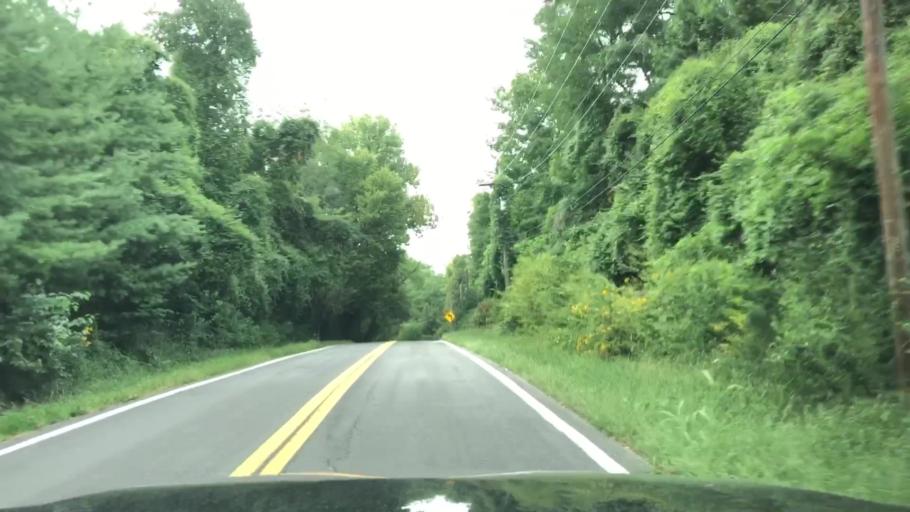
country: US
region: Missouri
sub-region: Saint Louis County
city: Hazelwood
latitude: 38.8147
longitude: -90.3735
